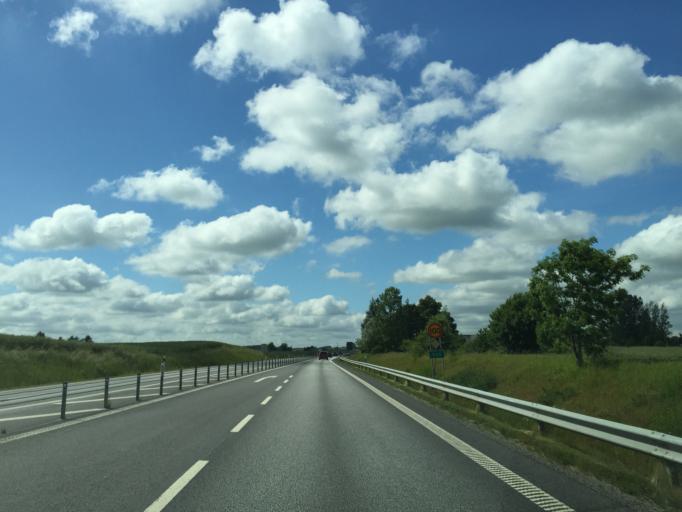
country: SE
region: Skane
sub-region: Skurups Kommun
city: Rydsgard
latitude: 55.4883
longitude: 13.5486
